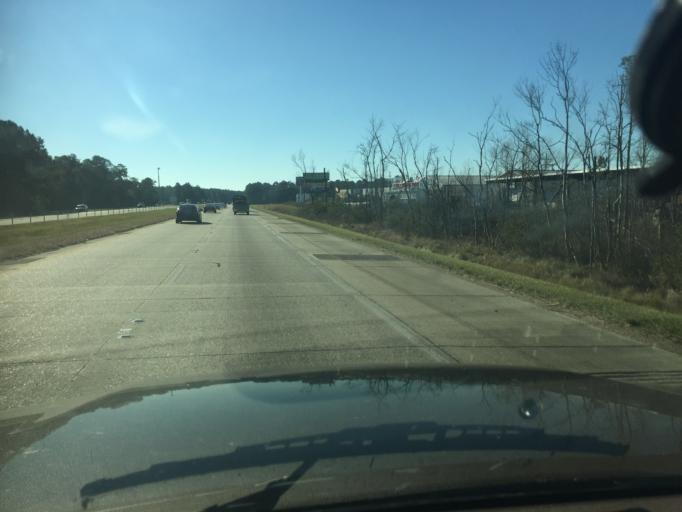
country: US
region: Louisiana
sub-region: Saint Tammany Parish
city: Pearl River
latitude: 30.3489
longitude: -89.7399
